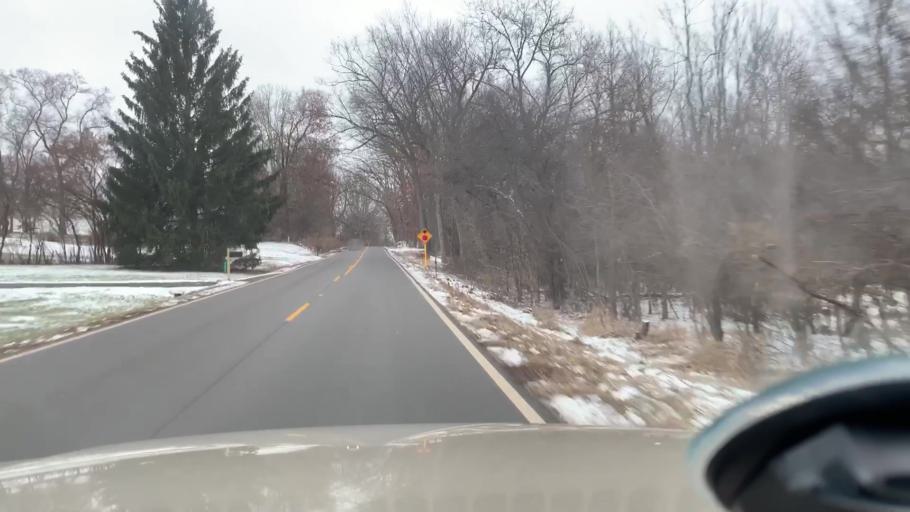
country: US
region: Michigan
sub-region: Jackson County
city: Spring Arbor
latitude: 42.2028
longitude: -84.5309
